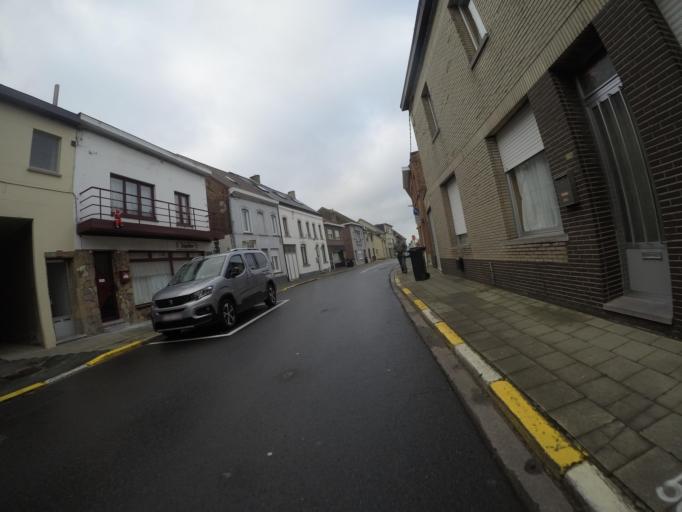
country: BE
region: Flanders
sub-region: Provincie Vlaams-Brabant
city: Liedekerke
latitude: 50.8678
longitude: 4.0951
